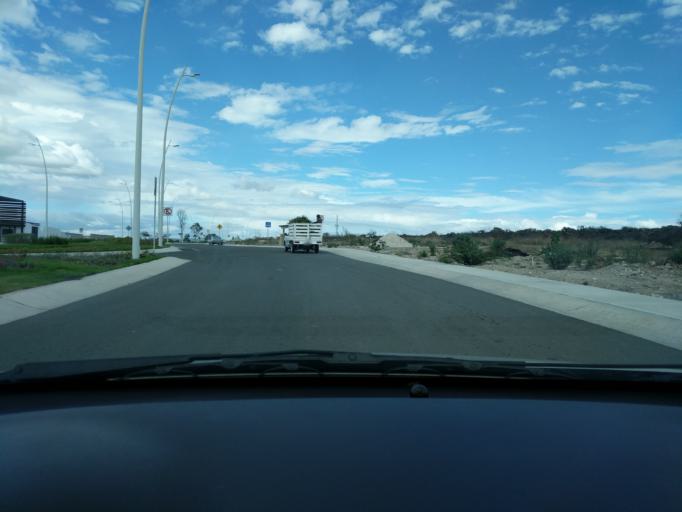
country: MX
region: Queretaro
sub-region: El Marques
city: El Pozo
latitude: 20.6443
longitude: -100.3142
